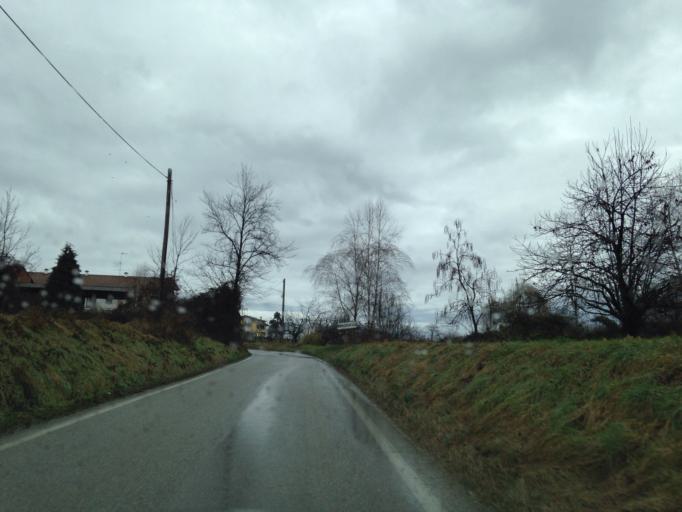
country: IT
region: Piedmont
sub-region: Provincia di Vercelli
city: Moncrivello
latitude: 45.3246
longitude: 7.9953
